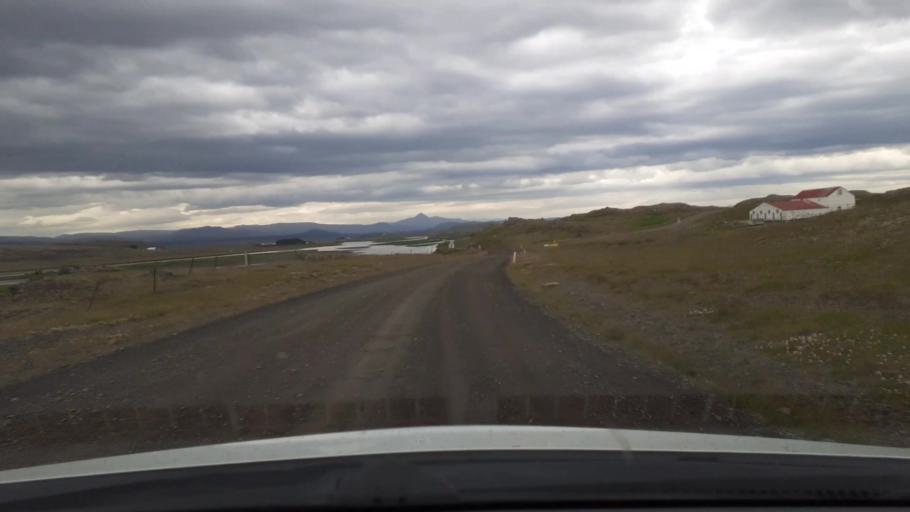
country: IS
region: West
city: Borgarnes
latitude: 64.5998
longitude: -21.6997
